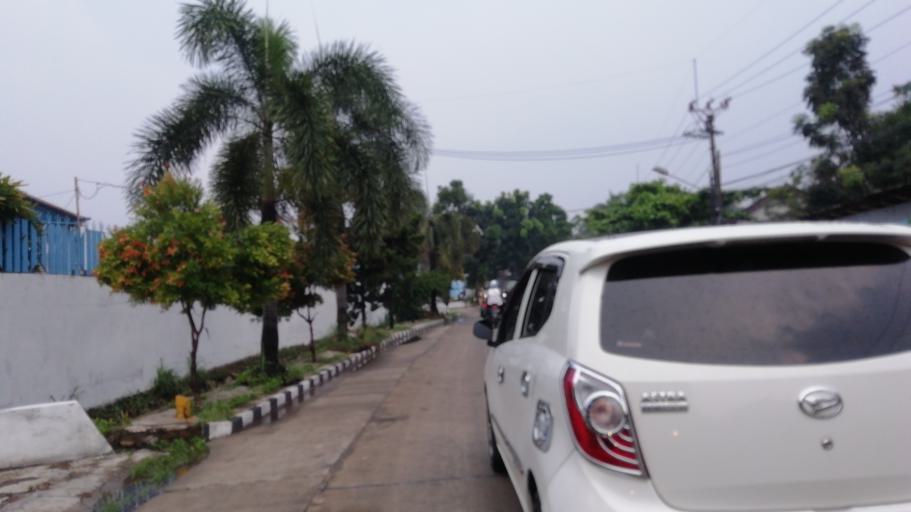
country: ID
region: West Java
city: Bogor
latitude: -6.5564
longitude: 106.8121
